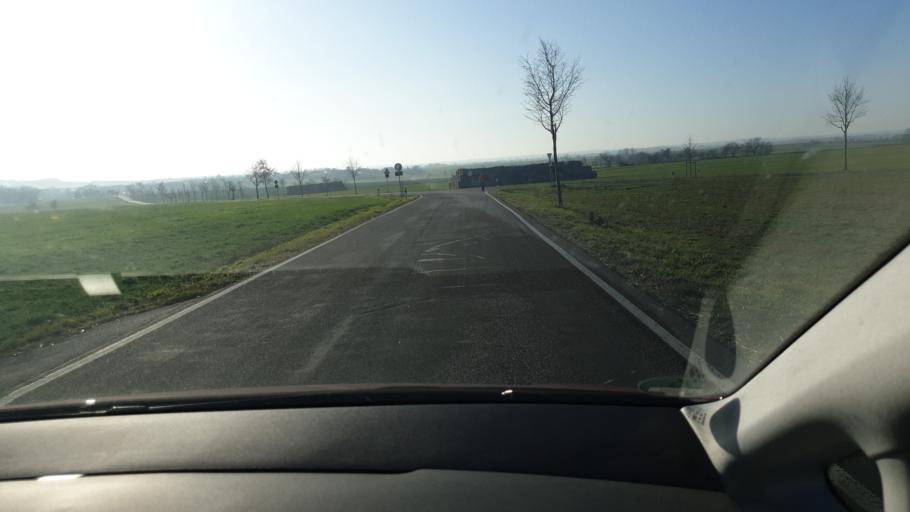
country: DE
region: Saxony
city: Hohburg
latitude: 51.4235
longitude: 12.7635
